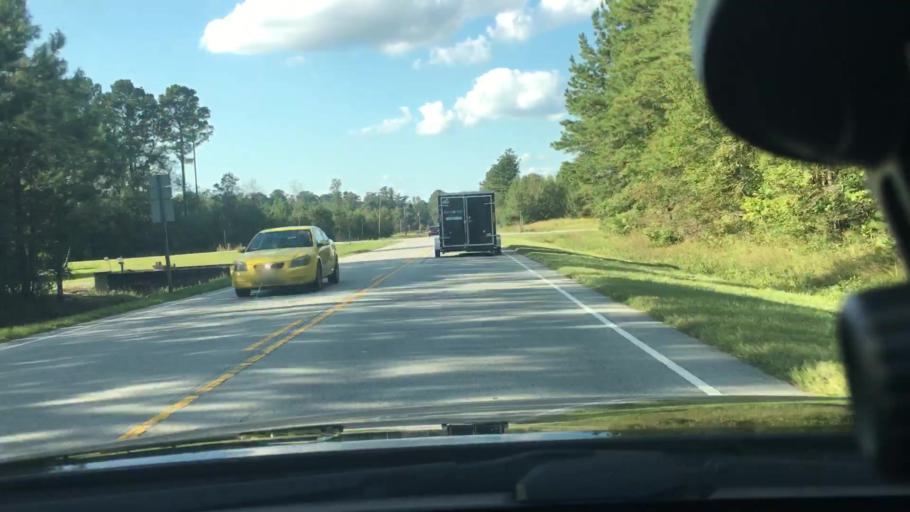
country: US
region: North Carolina
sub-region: Craven County
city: Vanceboro
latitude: 35.3263
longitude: -77.1478
